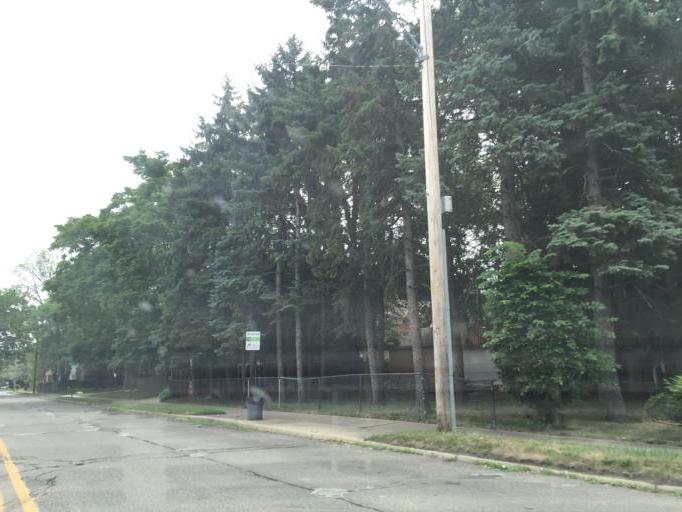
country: US
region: Michigan
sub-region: Wayne County
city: Redford
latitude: 42.4008
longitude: -83.2349
